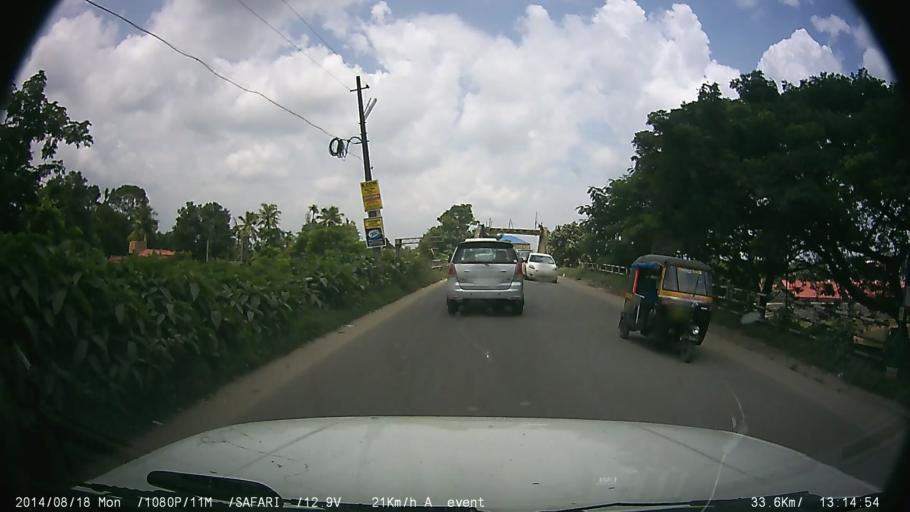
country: IN
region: Kerala
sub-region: Kottayam
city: Kottayam
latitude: 9.5972
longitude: 76.5258
